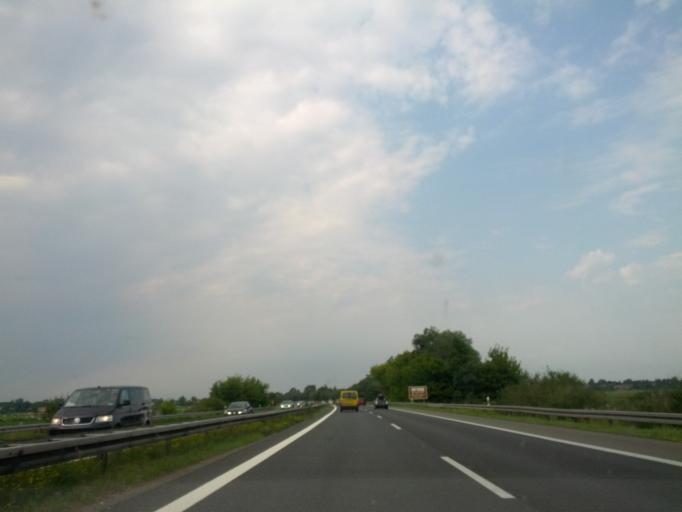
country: DE
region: Brandenburg
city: Fehrbellin
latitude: 52.8261
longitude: 12.7941
